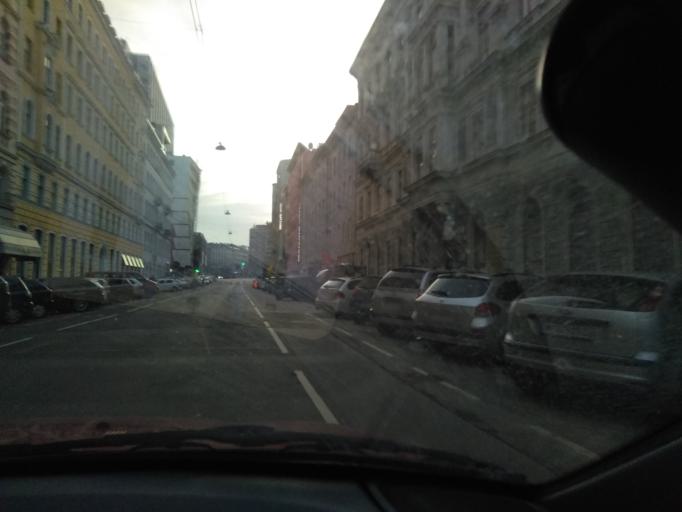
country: AT
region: Vienna
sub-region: Wien Stadt
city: Vienna
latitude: 48.2162
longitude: 16.3771
